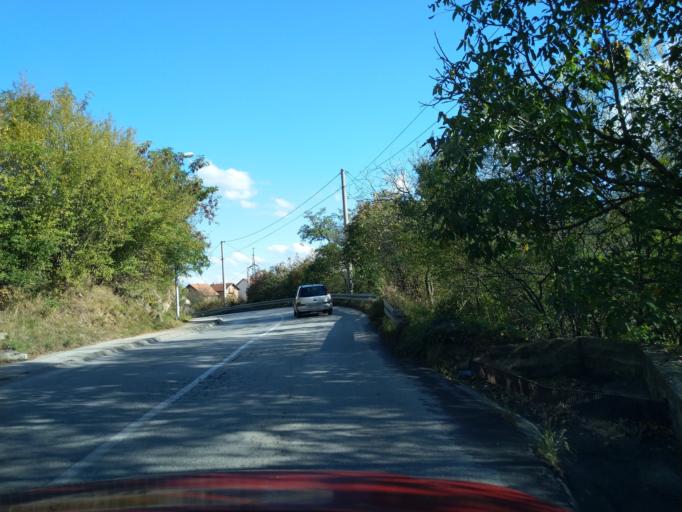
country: RS
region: Central Serbia
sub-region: Zlatiborski Okrug
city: Uzice
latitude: 43.8616
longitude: 19.8210
